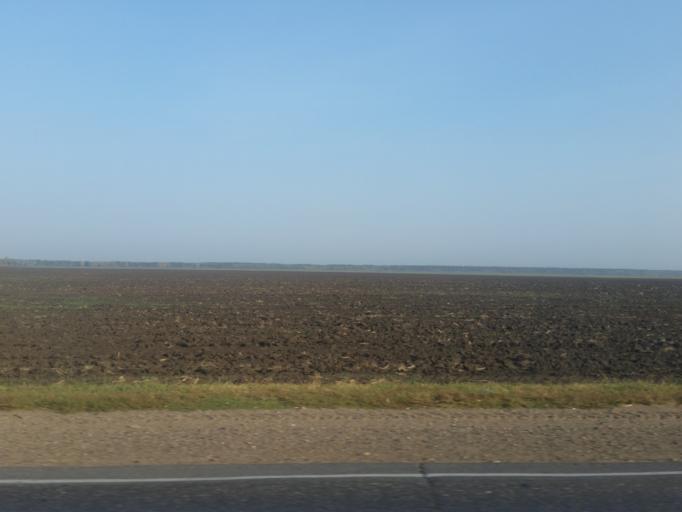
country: RU
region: Ulyanovsk
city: Mirnyy
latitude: 54.3732
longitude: 48.7455
